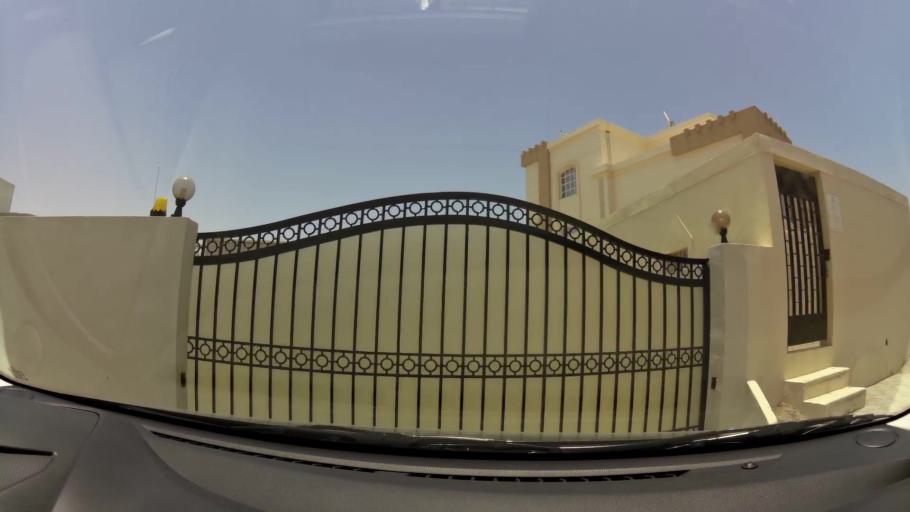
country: OM
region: Muhafazat Masqat
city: Bawshar
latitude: 23.5943
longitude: 58.4597
